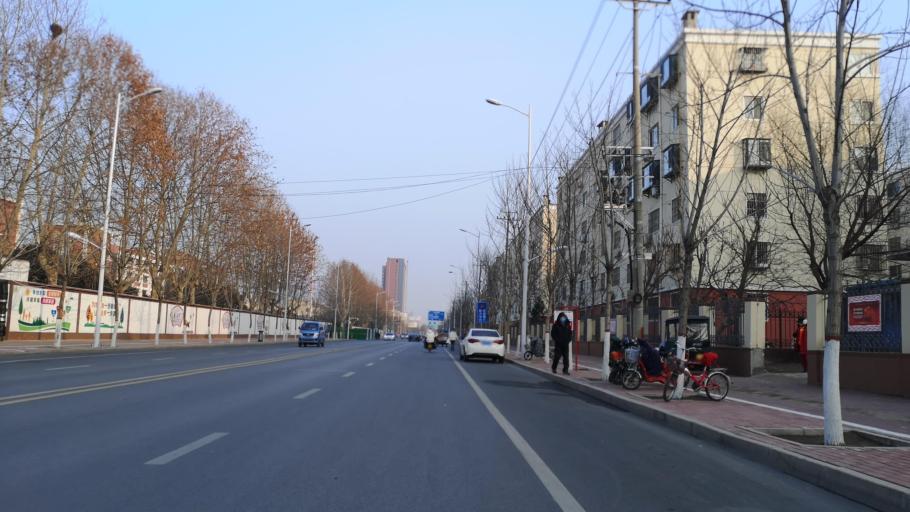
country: CN
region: Henan Sheng
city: Zhongyuanlu
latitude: 35.7636
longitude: 115.0595
